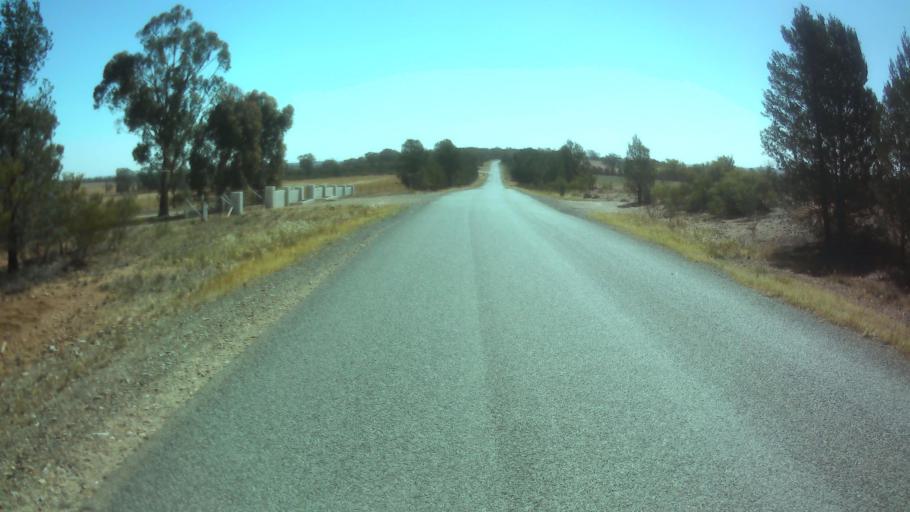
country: AU
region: New South Wales
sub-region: Weddin
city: Grenfell
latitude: -33.7545
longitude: 147.8357
